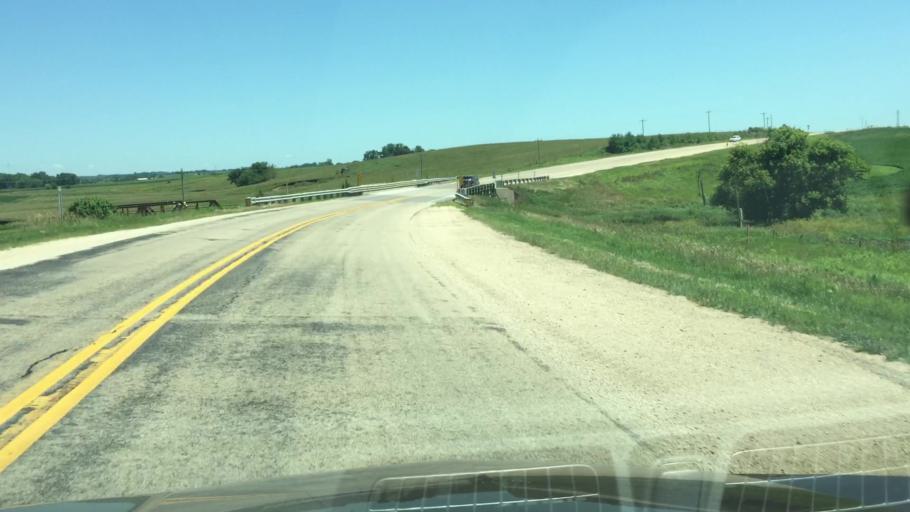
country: US
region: Iowa
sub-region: Cedar County
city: Mechanicsville
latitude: 41.9607
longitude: -91.1506
